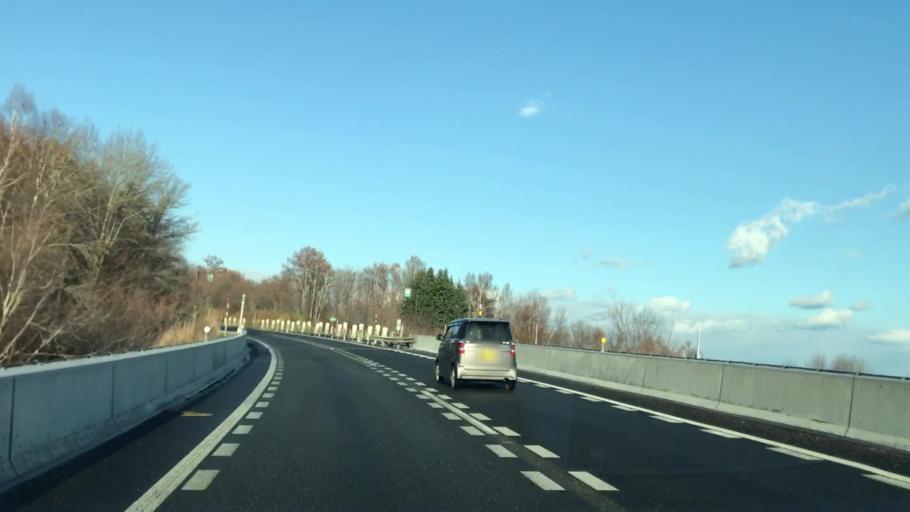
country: JP
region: Hokkaido
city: Otaru
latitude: 43.1509
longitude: 141.1275
